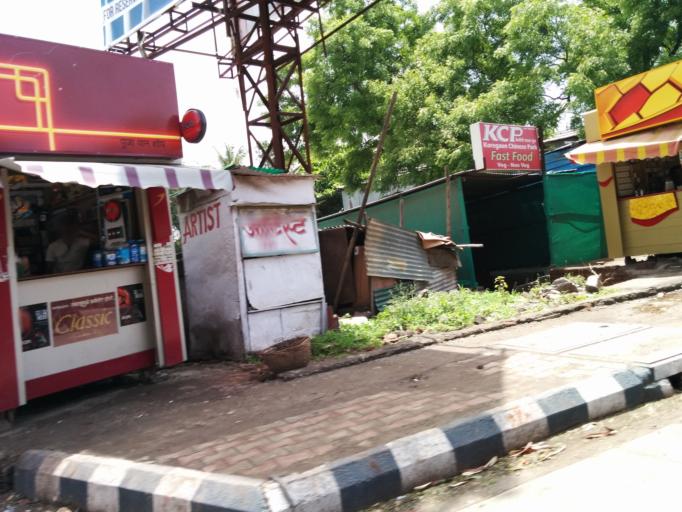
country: IN
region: Maharashtra
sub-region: Pune Division
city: Pune
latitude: 18.5372
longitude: 73.9086
